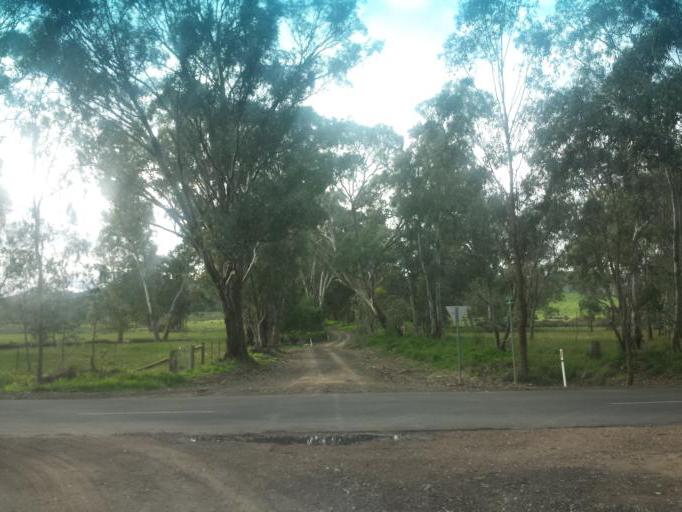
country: AU
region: Victoria
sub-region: Murrindindi
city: Kinglake West
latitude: -37.0231
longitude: 145.2501
